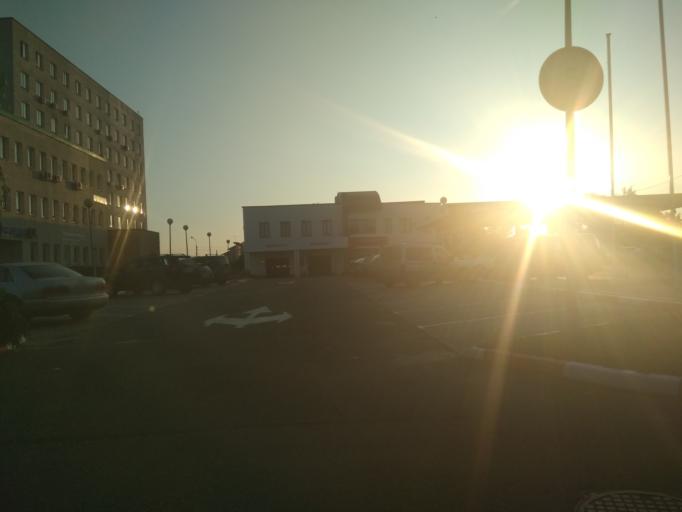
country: BY
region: Minsk
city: Minsk
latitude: 53.9330
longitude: 27.5562
